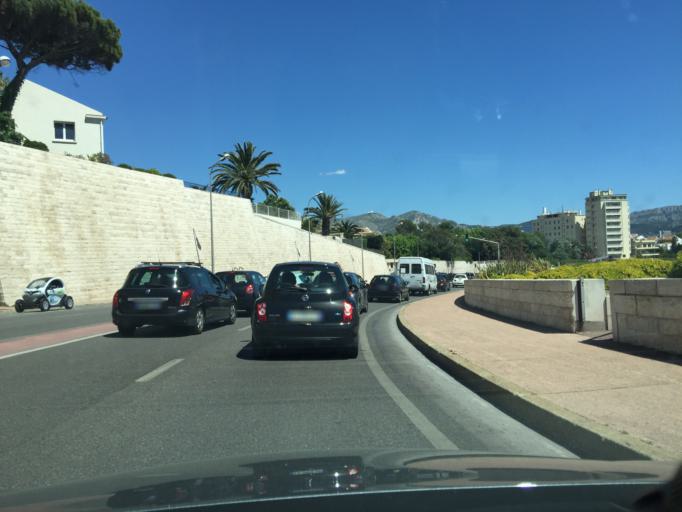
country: FR
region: Provence-Alpes-Cote d'Azur
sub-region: Departement des Bouches-du-Rhone
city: Marseille 08
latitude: 43.2689
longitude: 5.3693
